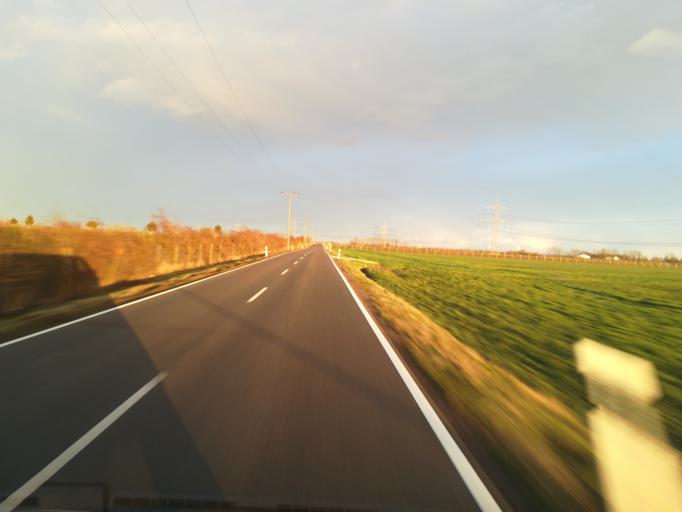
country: DE
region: Saxony-Anhalt
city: Brehna
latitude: 51.5154
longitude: 12.2130
